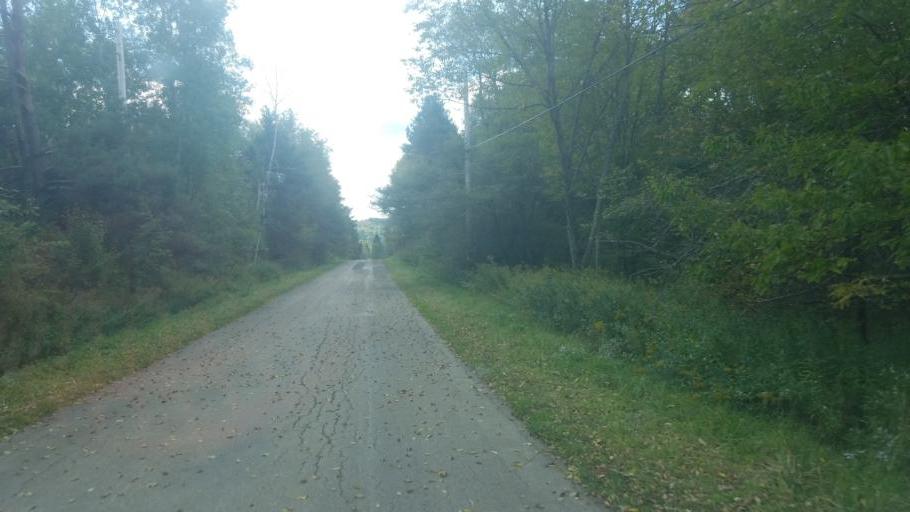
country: US
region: New York
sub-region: Cattaraugus County
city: Franklinville
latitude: 42.2212
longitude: -78.4145
